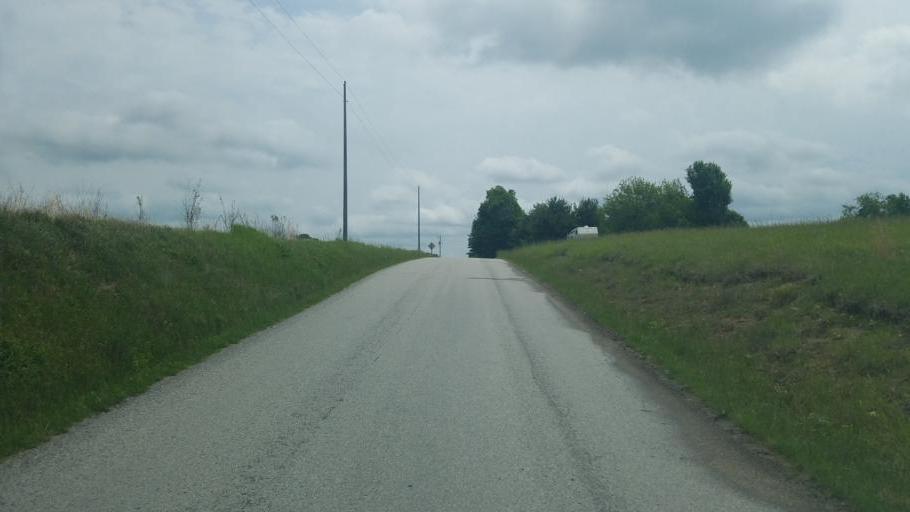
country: US
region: Ohio
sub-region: Licking County
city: Johnstown
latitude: 40.1381
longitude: -82.6123
